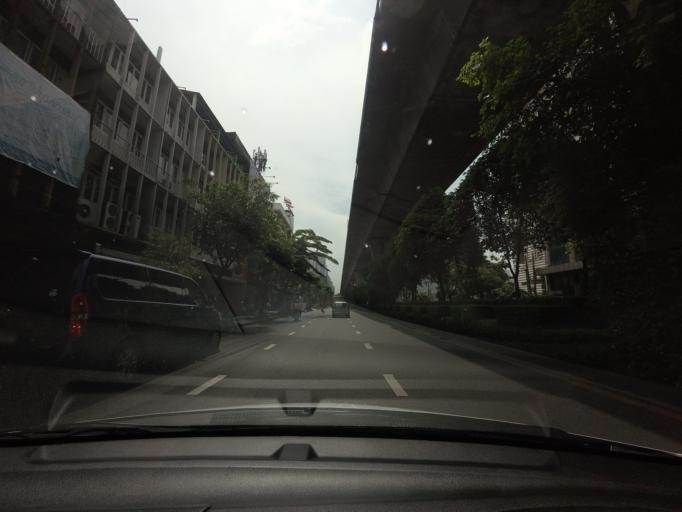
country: TH
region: Bangkok
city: Watthana
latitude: 13.7166
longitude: 100.5892
